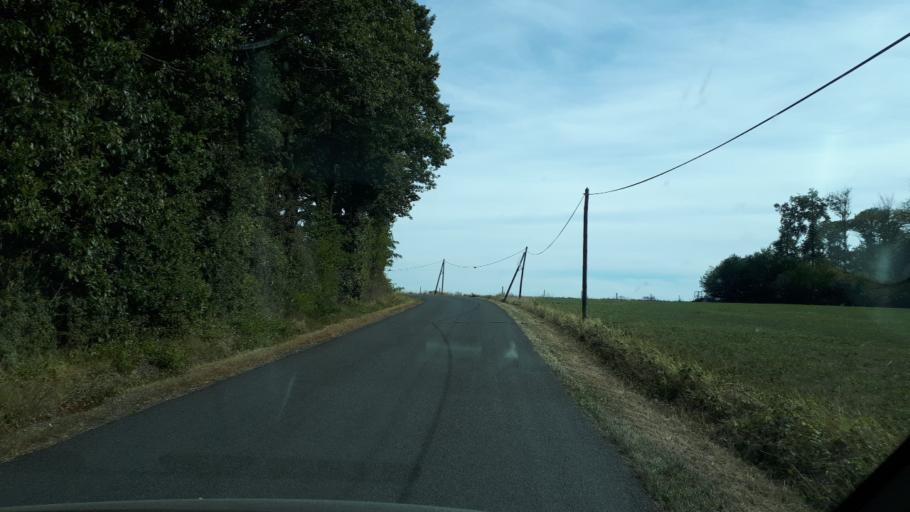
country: FR
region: Centre
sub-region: Departement du Loir-et-Cher
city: Montoire-sur-le-Loir
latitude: 47.7147
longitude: 0.8282
